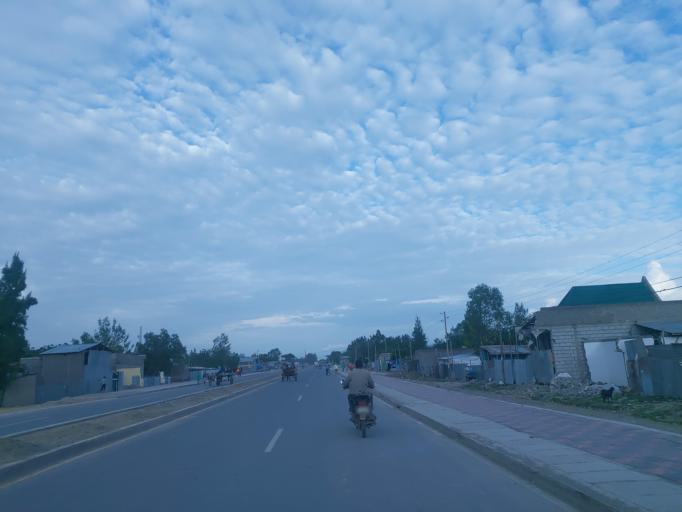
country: ET
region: Oromiya
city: Ziway
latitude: 8.1454
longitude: 38.8082
